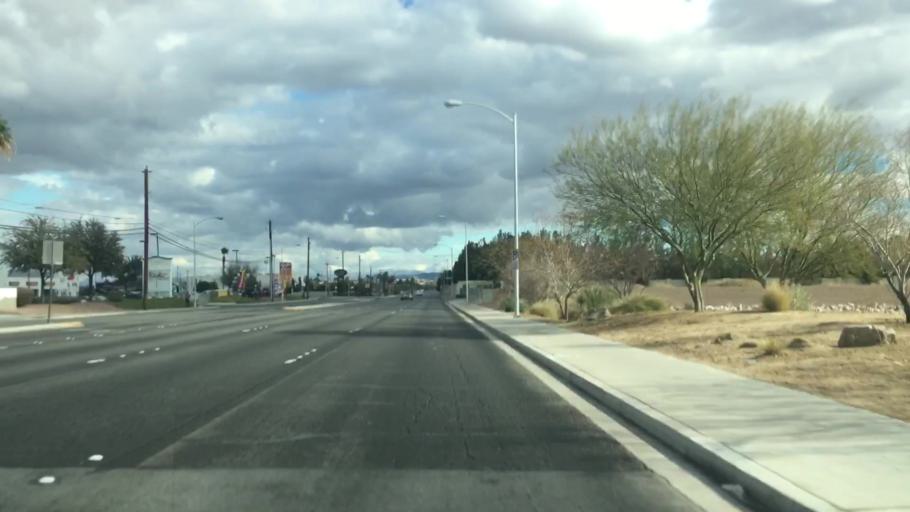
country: US
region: Nevada
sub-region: Clark County
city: Whitney
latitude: 36.0715
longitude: -115.1067
